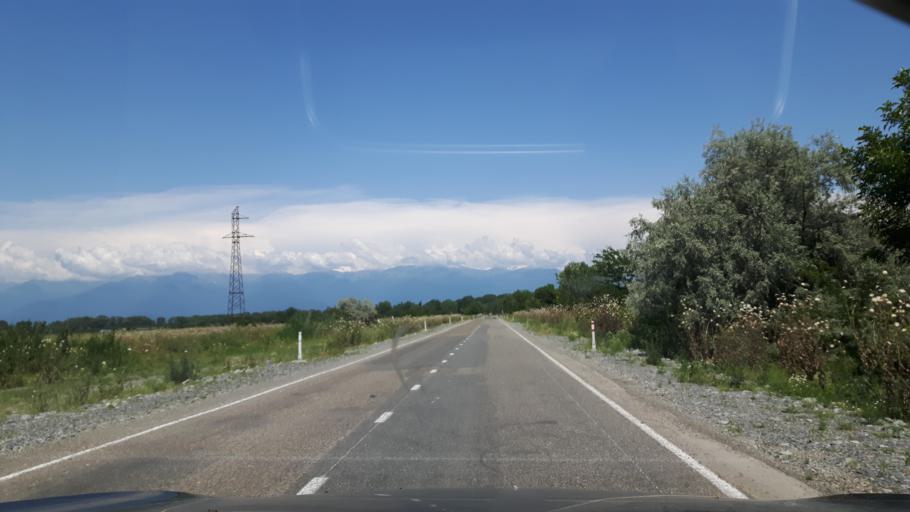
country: GE
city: Tsnori
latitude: 41.6606
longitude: 46.0714
